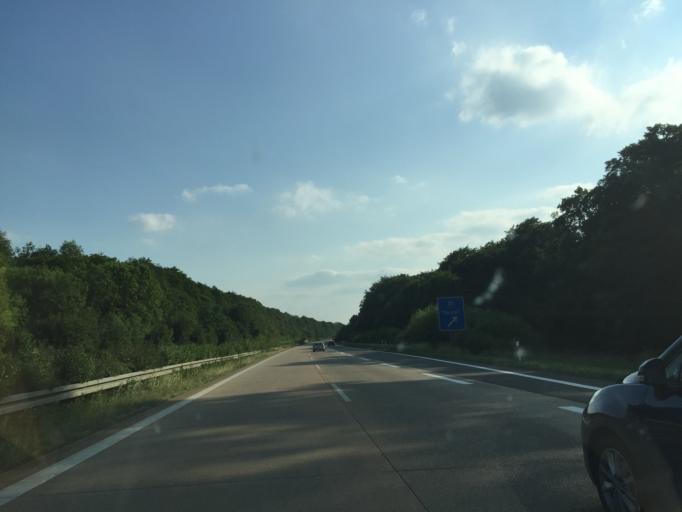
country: DE
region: Baden-Wuerttemberg
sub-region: Karlsruhe Region
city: Osterburken
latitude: 49.3826
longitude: 9.4628
